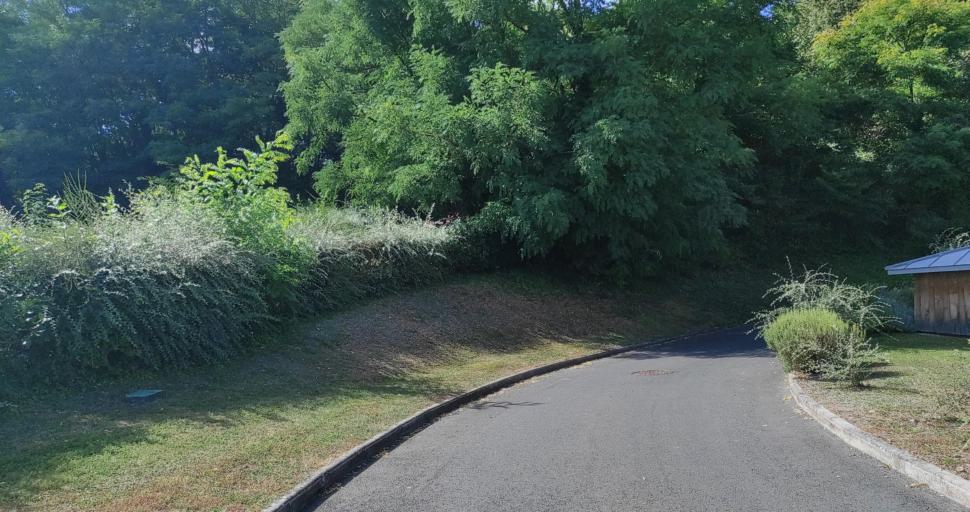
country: FR
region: Midi-Pyrenees
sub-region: Departement de l'Aveyron
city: Cransac
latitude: 44.5291
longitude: 2.2753
